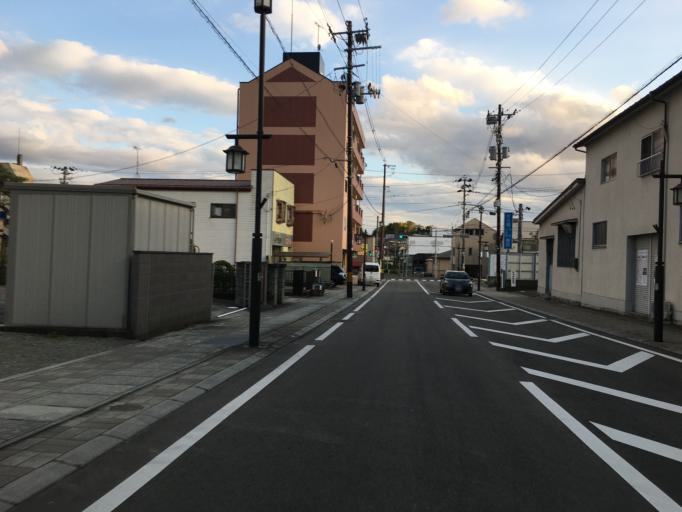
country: JP
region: Fukushima
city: Nihommatsu
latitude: 37.5917
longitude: 140.4338
